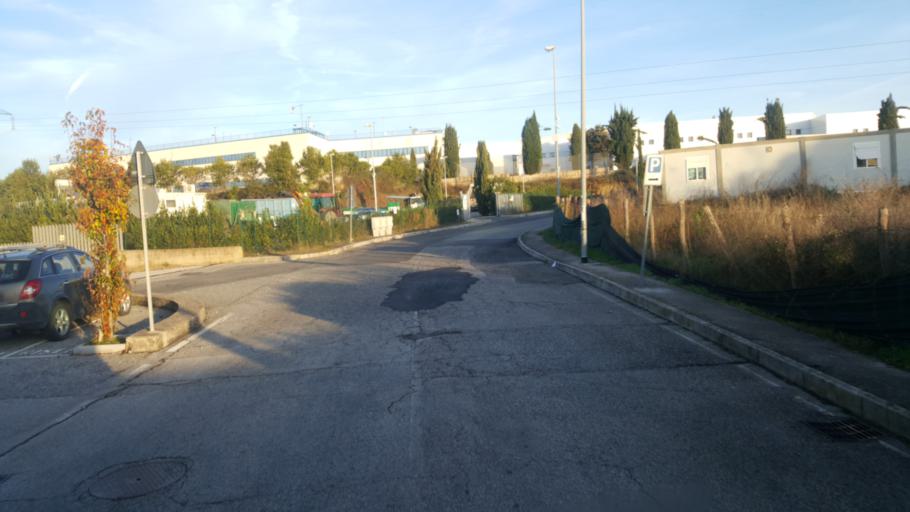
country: IT
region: Latium
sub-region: Citta metropolitana di Roma Capitale
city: Formello
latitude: 42.0525
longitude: 12.3994
